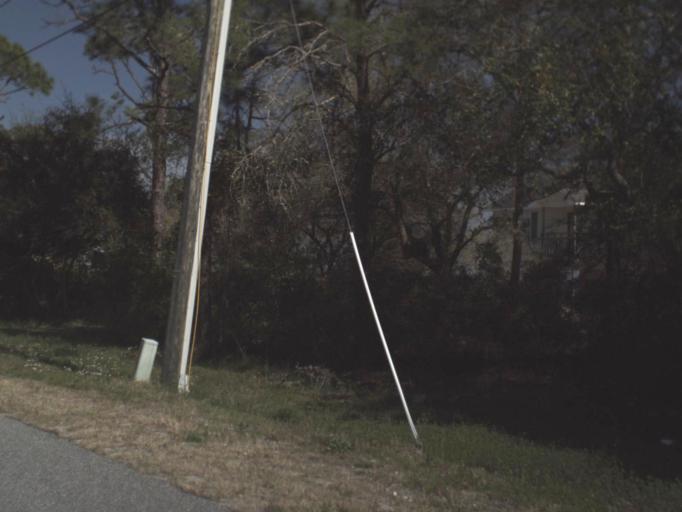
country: US
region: Florida
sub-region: Franklin County
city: Carrabelle
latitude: 29.8110
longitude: -84.7228
